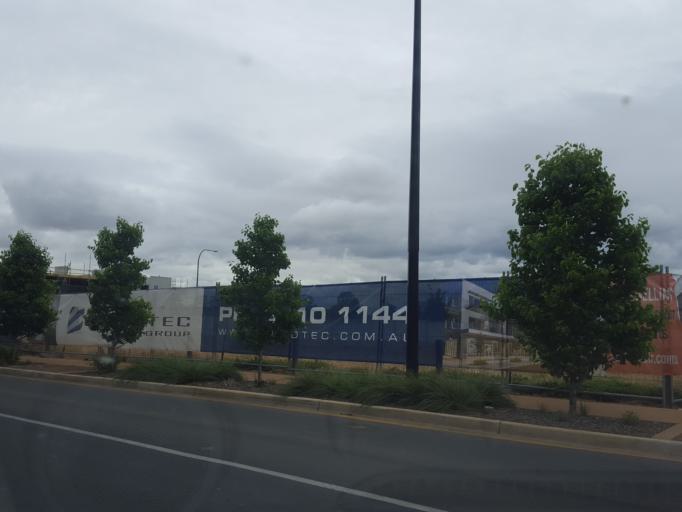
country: AU
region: South Australia
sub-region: Charles Sturt
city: Albert Park
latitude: -34.8691
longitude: 138.5305
